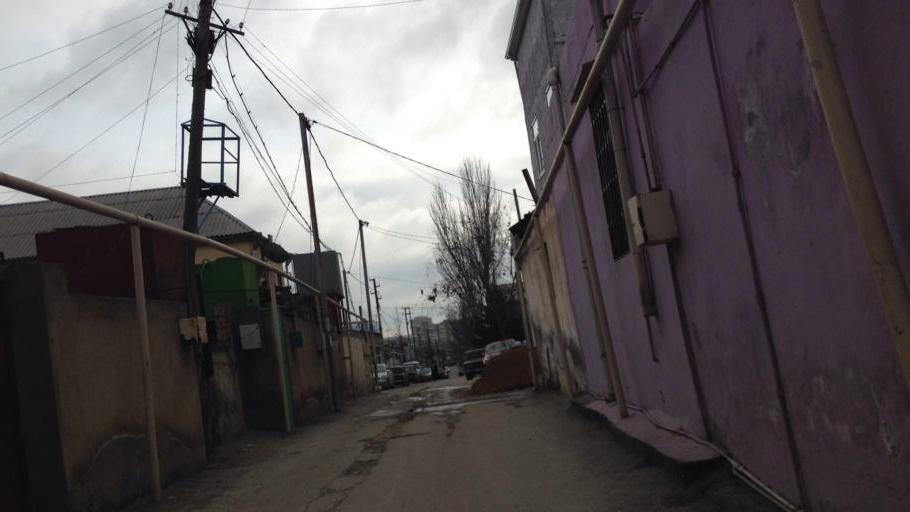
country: AZ
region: Baki
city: Bilajari
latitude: 40.4025
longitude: 49.8269
